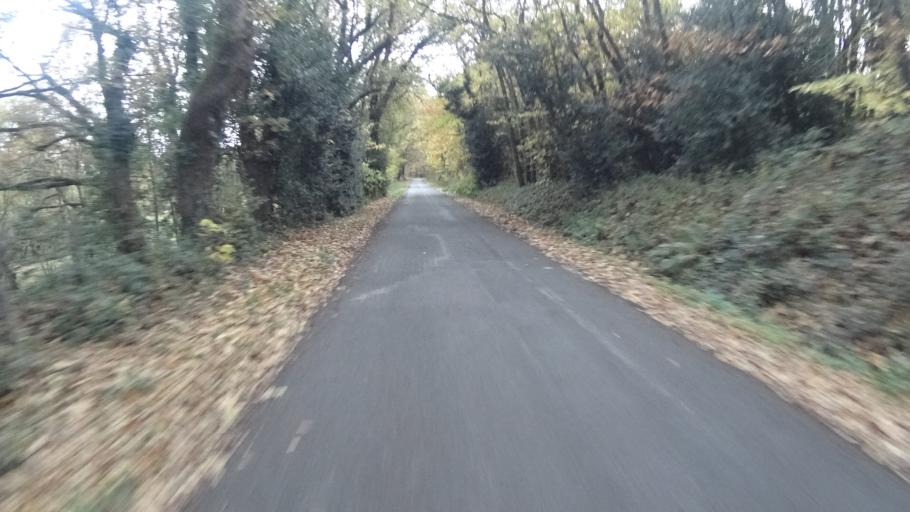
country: FR
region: Pays de la Loire
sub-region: Departement de la Loire-Atlantique
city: Saint-Nicolas-de-Redon
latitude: 47.6648
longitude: -2.0535
